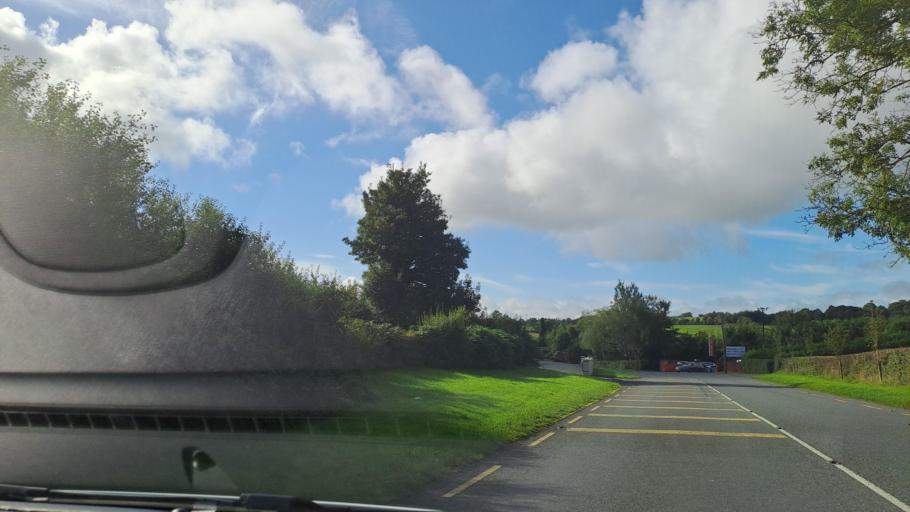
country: IE
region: Ulster
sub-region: An Cabhan
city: Kingscourt
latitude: 53.9389
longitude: -6.7793
